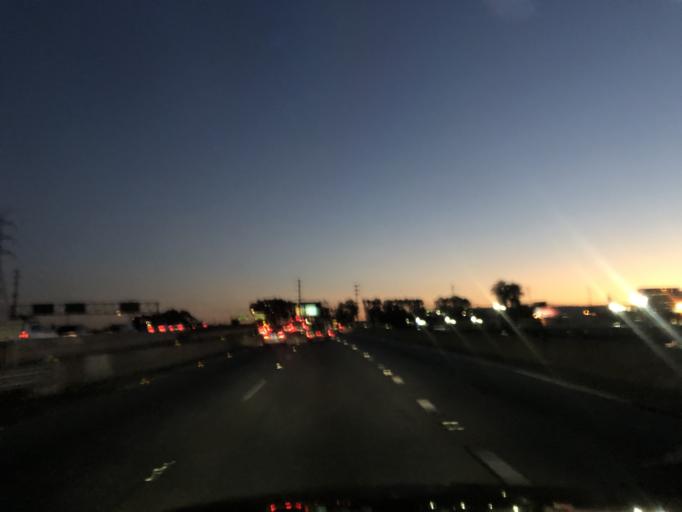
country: US
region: California
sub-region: Los Angeles County
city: Carson
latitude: 33.8633
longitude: -118.2854
